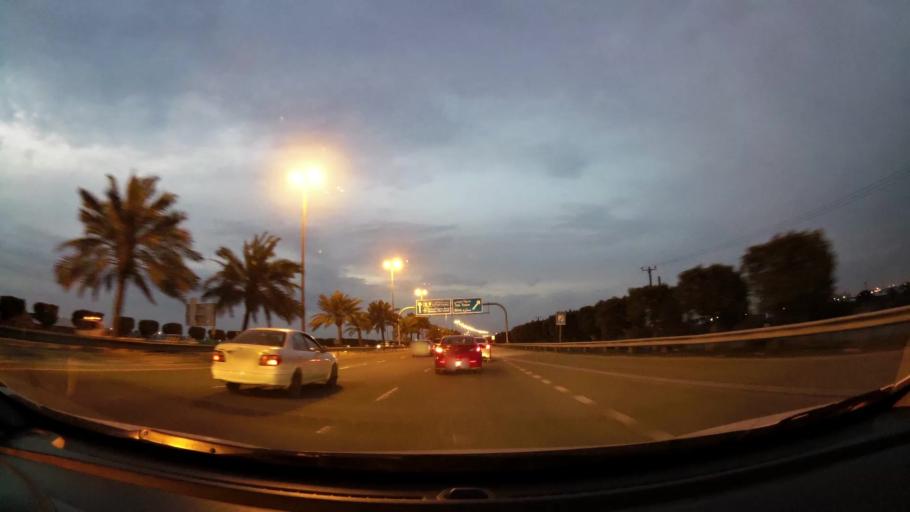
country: BH
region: Northern
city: Madinat `Isa
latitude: 26.1701
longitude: 50.5029
